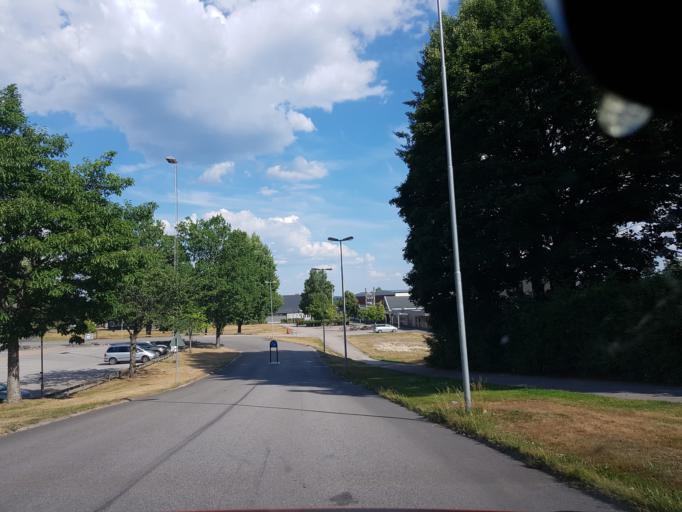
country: SE
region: Joenkoeping
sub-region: Gislaveds Kommun
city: Gislaved
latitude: 57.2951
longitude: 13.5302
